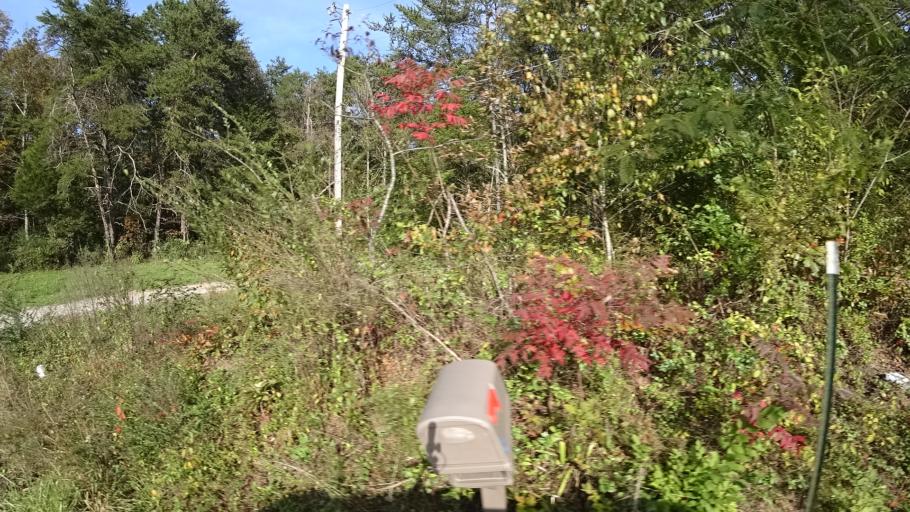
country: US
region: Tennessee
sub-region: Knox County
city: Farragut
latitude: 35.9153
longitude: -84.1767
